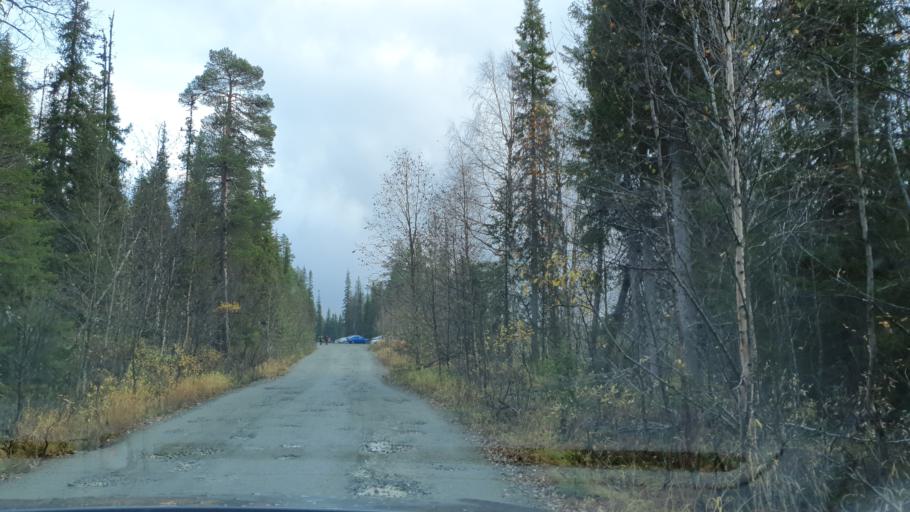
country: FI
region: Lapland
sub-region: Tunturi-Lappi
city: Kolari
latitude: 67.6045
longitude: 24.2134
